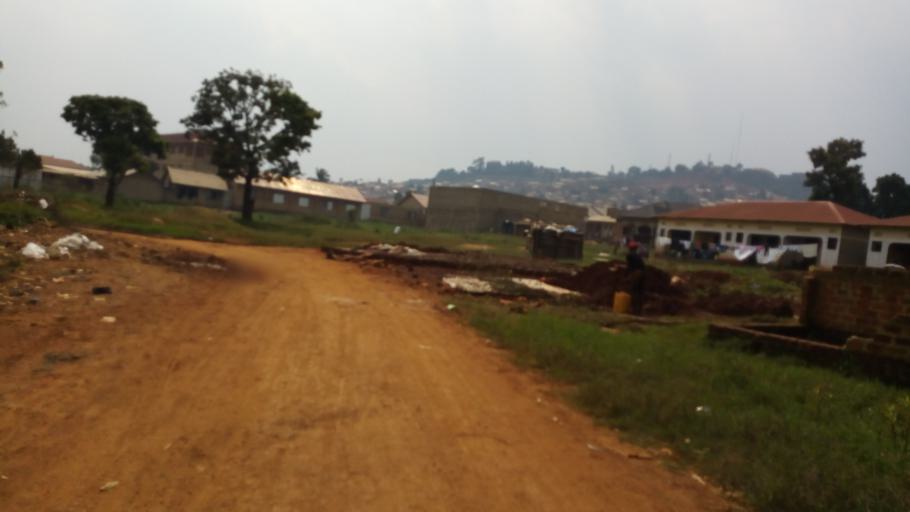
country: UG
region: Central Region
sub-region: Wakiso District
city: Kireka
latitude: 0.3271
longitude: 32.6452
